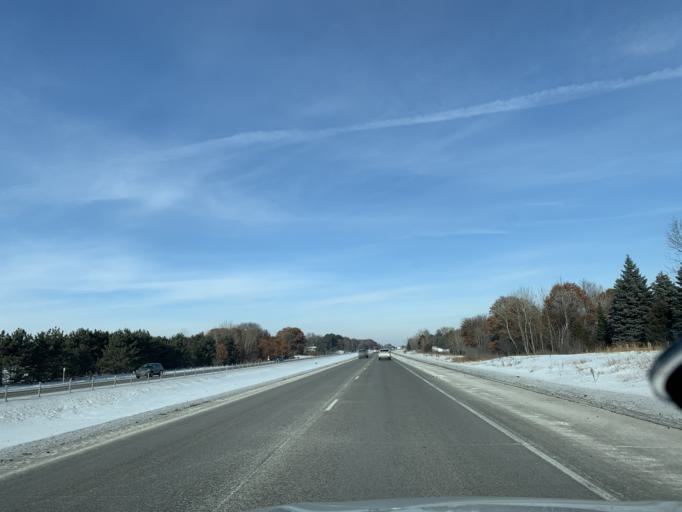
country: US
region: Minnesota
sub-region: Chisago County
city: Wyoming
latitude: 45.3078
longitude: -93.0029
